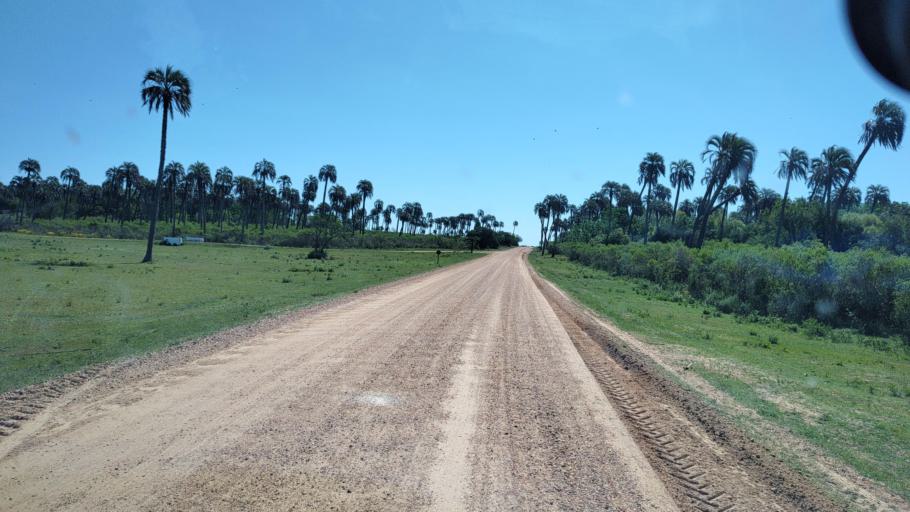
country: AR
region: Entre Rios
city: Ubajay
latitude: -31.8744
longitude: -58.2300
